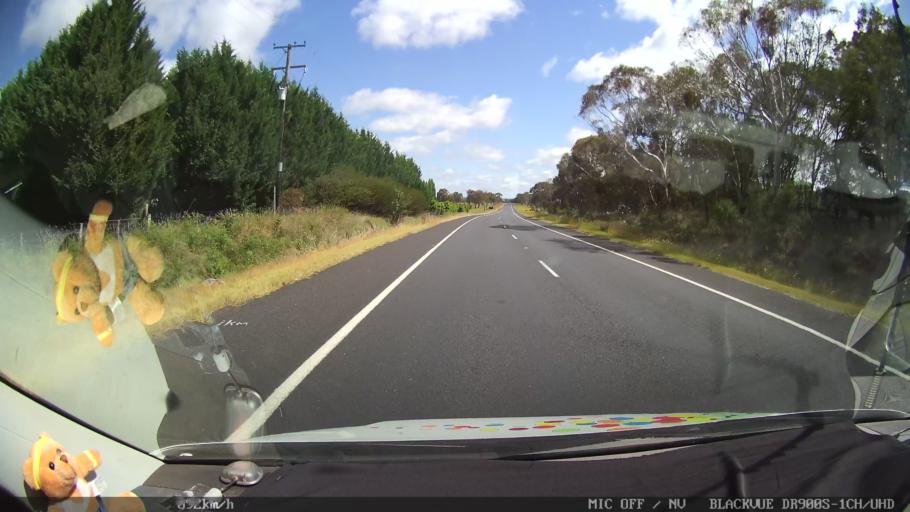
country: AU
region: New South Wales
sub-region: Glen Innes Severn
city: Glen Innes
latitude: -29.8771
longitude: 151.7342
